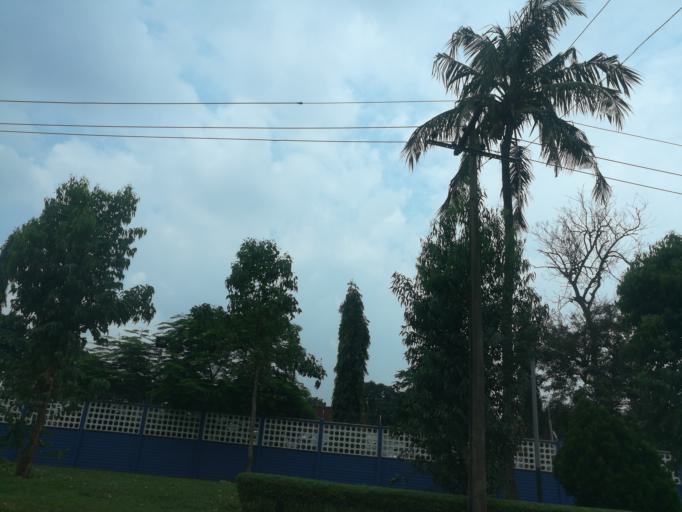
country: NG
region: Lagos
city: Ojota
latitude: 6.6033
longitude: 3.3693
